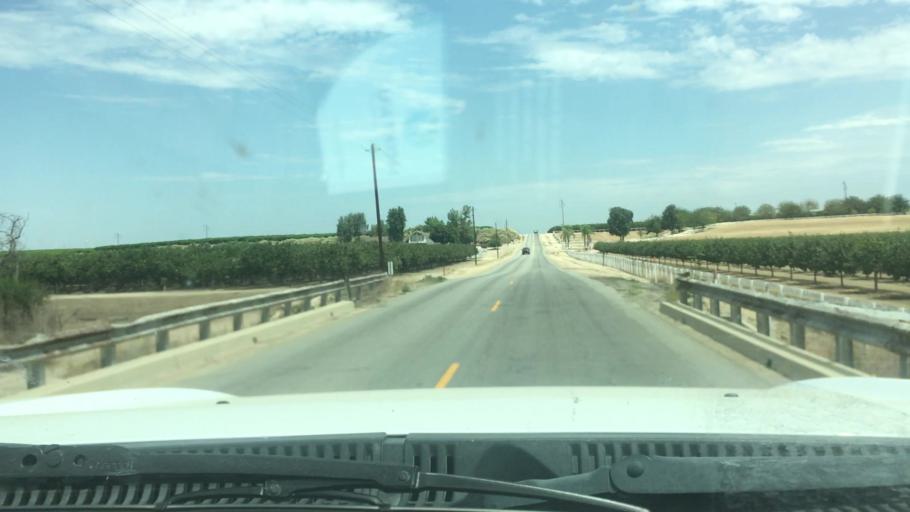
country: US
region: California
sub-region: Kern County
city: Shafter
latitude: 35.5628
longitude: -119.1512
